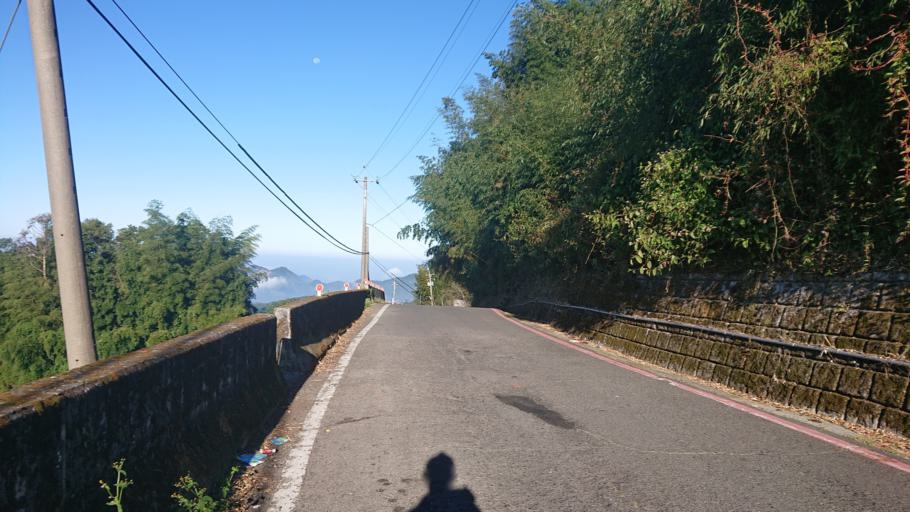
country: TW
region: Taiwan
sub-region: Chiayi
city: Jiayi Shi
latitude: 23.4781
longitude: 120.7017
